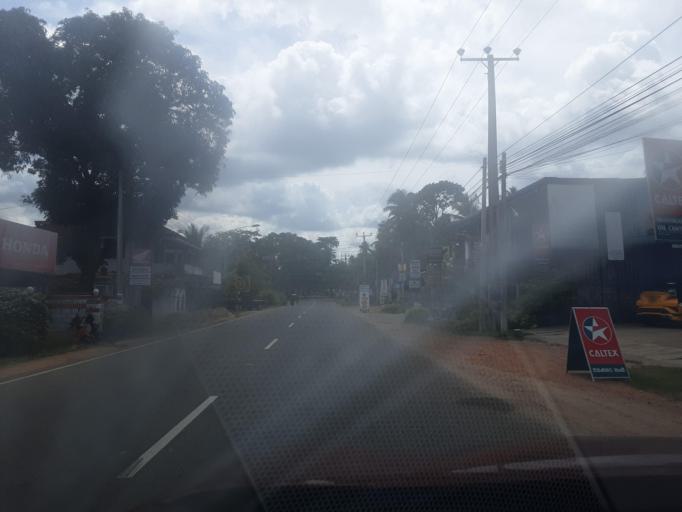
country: LK
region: North Western
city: Kuliyapitiya
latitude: 7.4739
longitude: 80.0173
